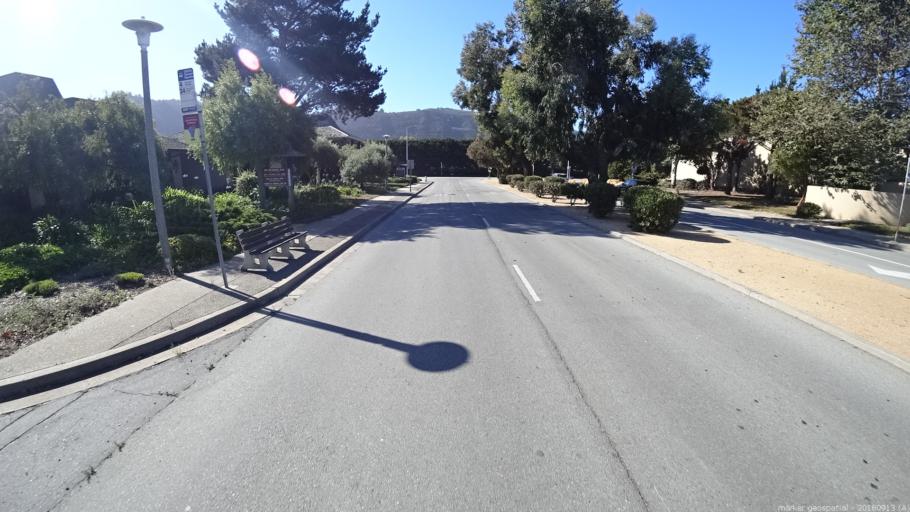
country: US
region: California
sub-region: Monterey County
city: Carmel-by-the-Sea
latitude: 36.5388
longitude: -121.9048
